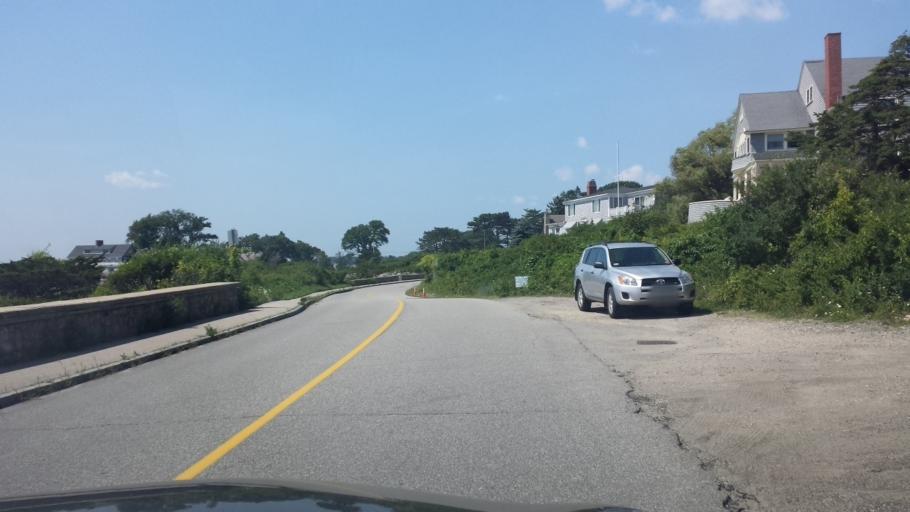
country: US
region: Maine
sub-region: York County
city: Kennebunkport
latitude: 43.3420
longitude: -70.4683
